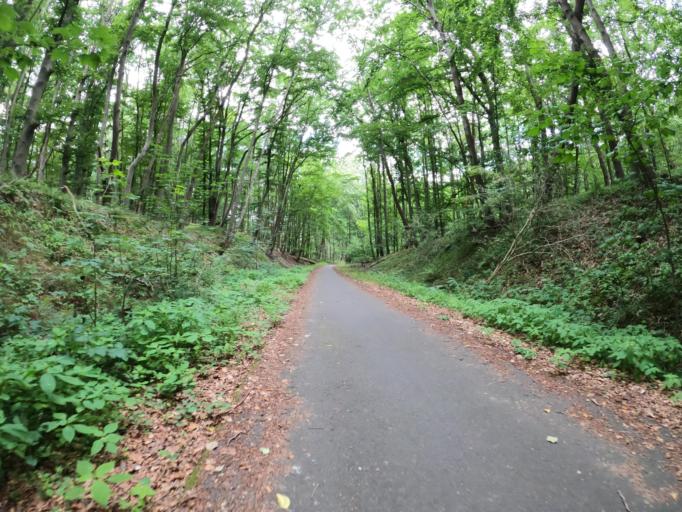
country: DE
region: Mecklenburg-Vorpommern
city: Woldegk
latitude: 53.3583
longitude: 13.5915
